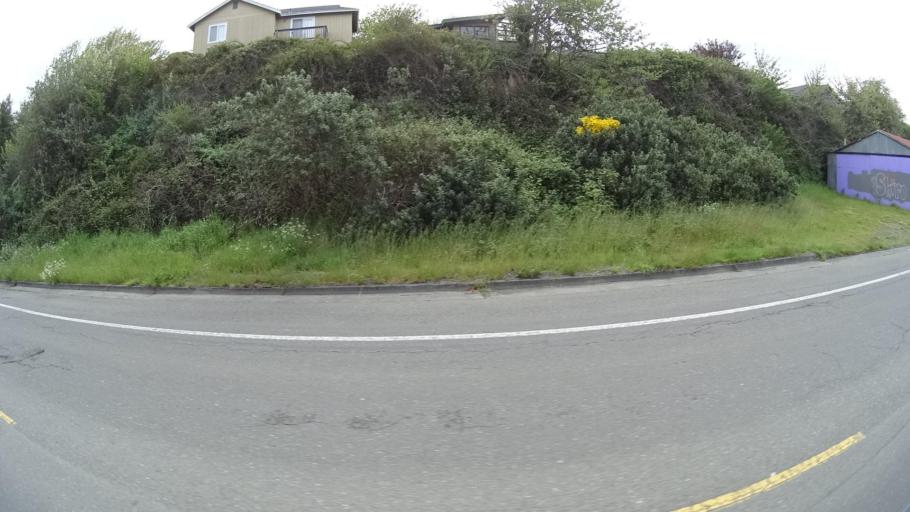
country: US
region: California
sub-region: Humboldt County
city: Arcata
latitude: 40.8816
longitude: -124.0918
